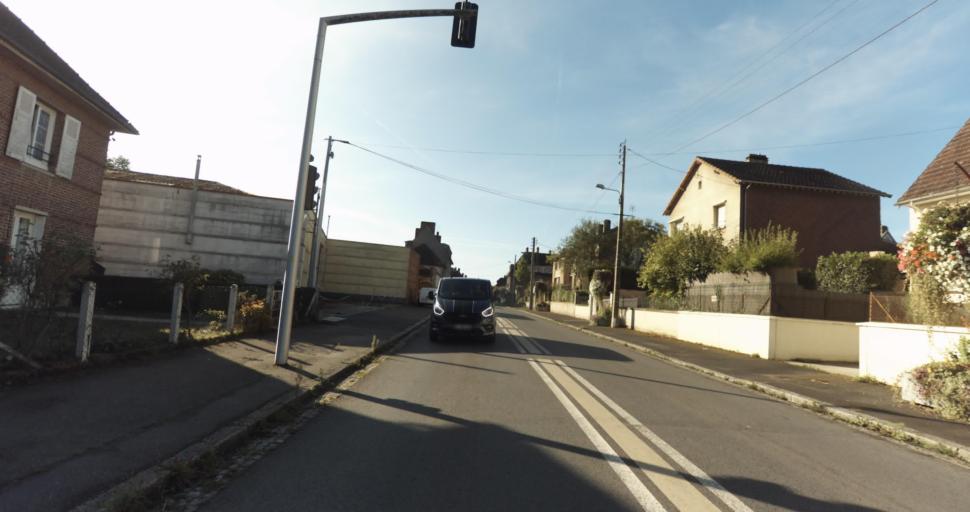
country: FR
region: Lower Normandy
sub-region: Departement de l'Orne
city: Vimoutiers
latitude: 48.9293
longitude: 0.1958
